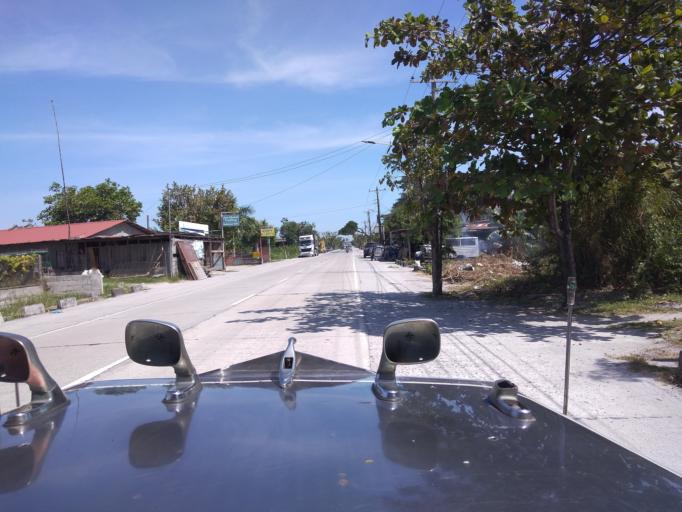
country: PH
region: Central Luzon
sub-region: Province of Pampanga
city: San Juan
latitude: 15.0175
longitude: 120.6690
